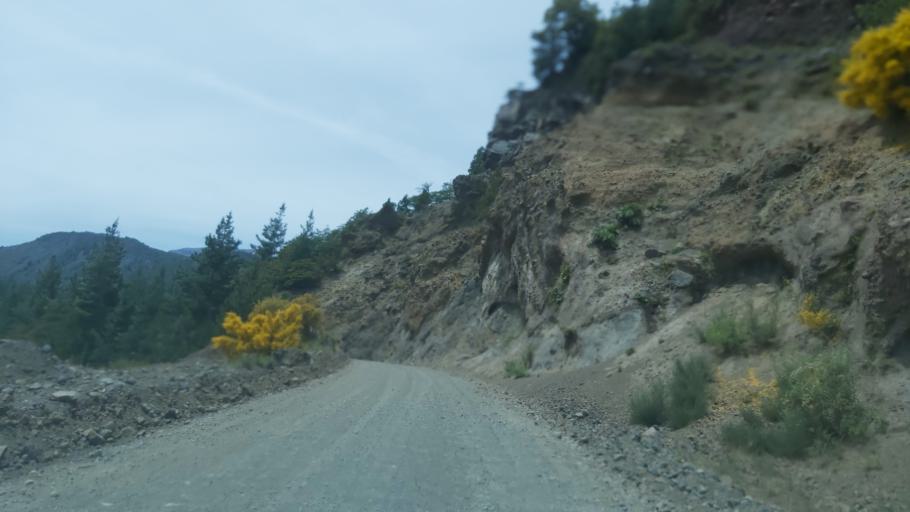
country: AR
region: Neuquen
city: Las Ovejas
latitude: -37.3935
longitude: -71.4617
